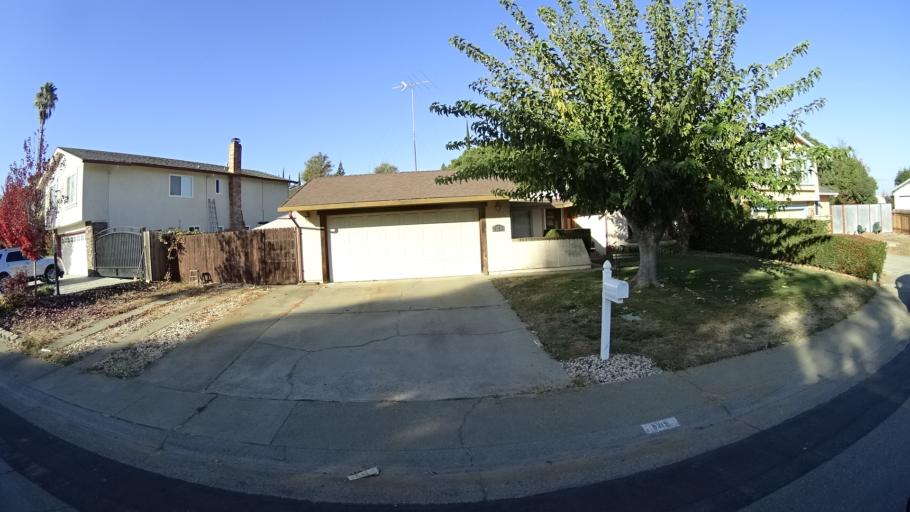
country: US
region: California
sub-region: Sacramento County
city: Citrus Heights
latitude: 38.7140
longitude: -121.2551
